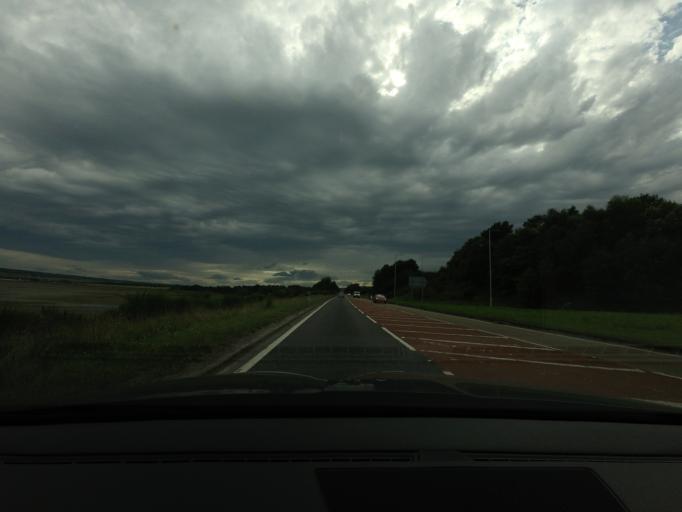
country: GB
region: Scotland
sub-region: Highland
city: Evanton
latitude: 57.6775
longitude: -4.2985
